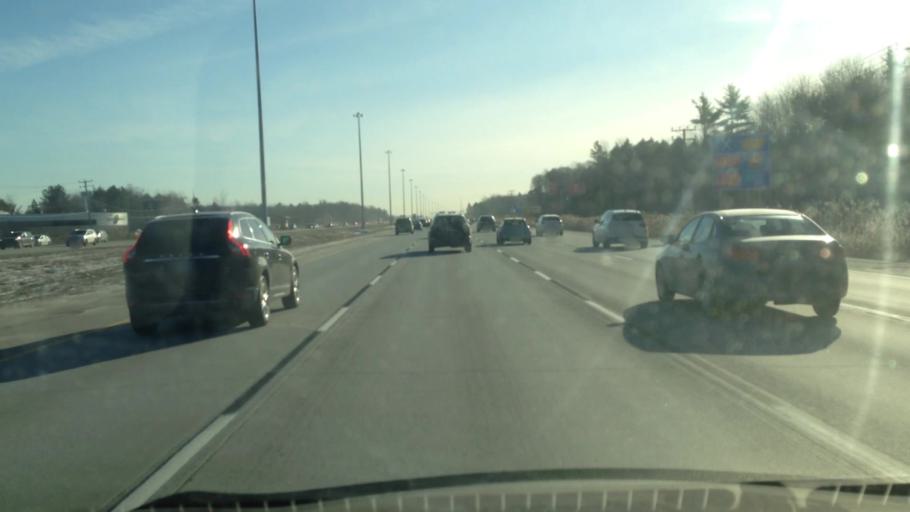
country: CA
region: Quebec
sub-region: Laurentides
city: Blainville
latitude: 45.6633
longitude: -73.8927
